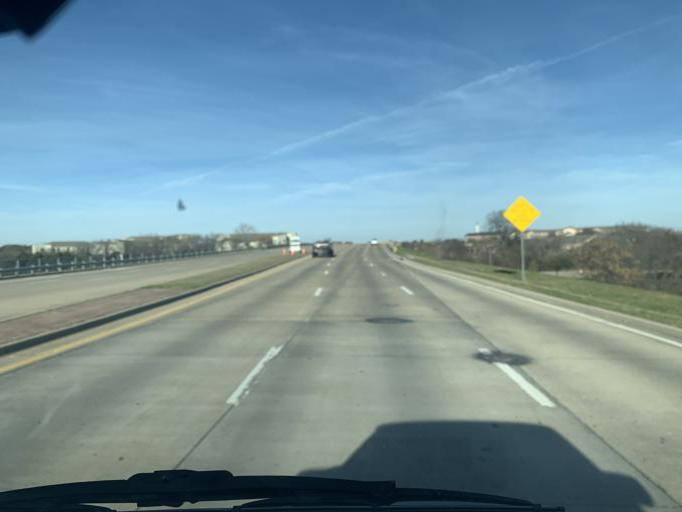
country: US
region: Texas
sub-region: Dallas County
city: Cedar Hill
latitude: 32.6014
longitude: -96.9456
